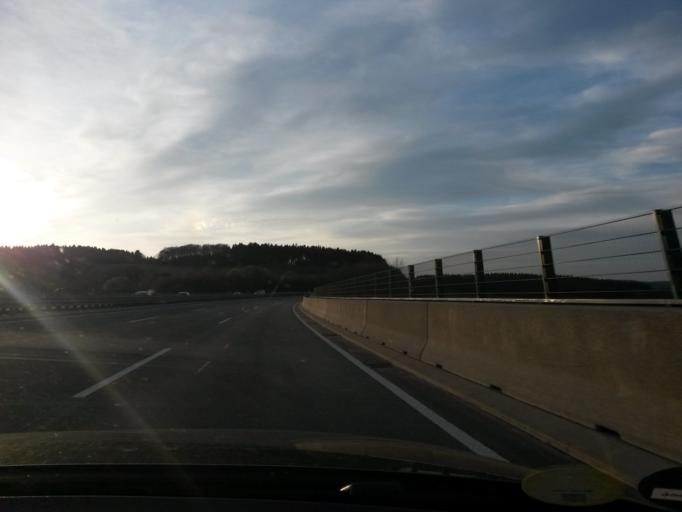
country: DE
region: North Rhine-Westphalia
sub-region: Regierungsbezirk Arnsberg
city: Drolshagen
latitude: 51.0561
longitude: 7.7254
